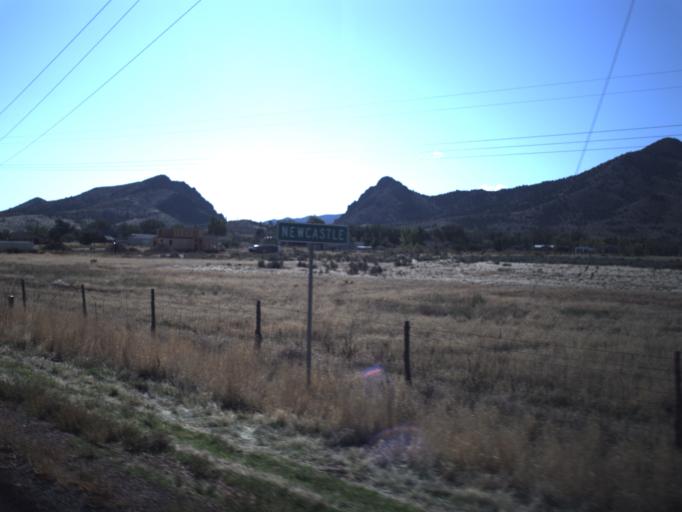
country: US
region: Utah
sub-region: Washington County
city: Enterprise
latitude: 37.6726
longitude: -113.5532
